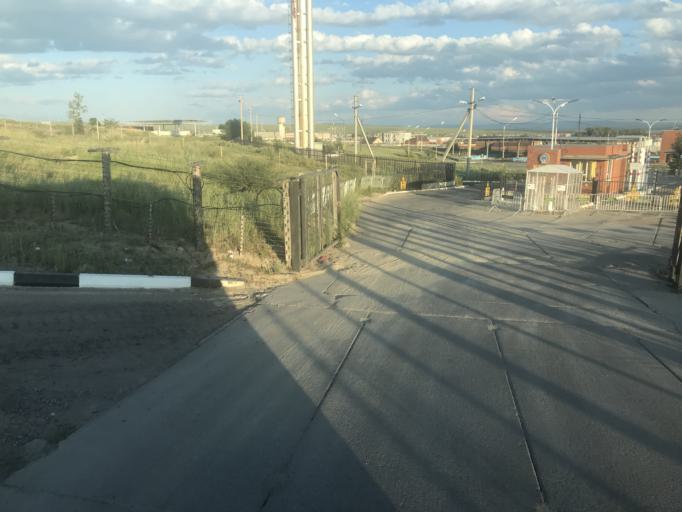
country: MN
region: Selenge
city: Altanbulag
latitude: 50.3236
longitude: 106.4892
